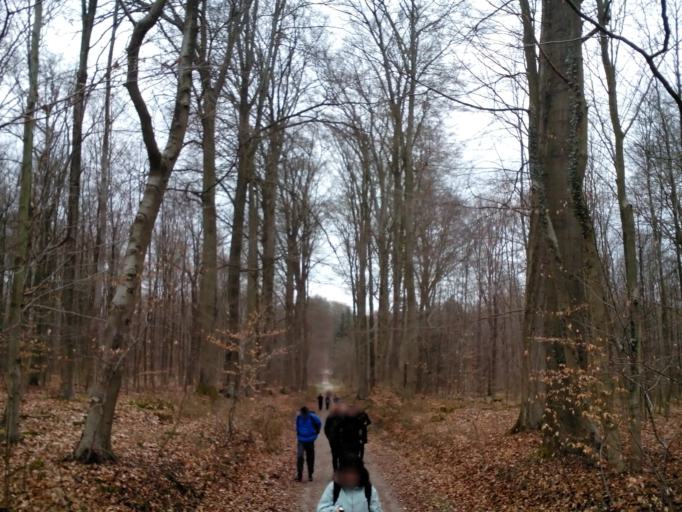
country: BE
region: Flanders
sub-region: Provincie Vlaams-Brabant
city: Oud-Heverlee
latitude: 50.8039
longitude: 4.6832
